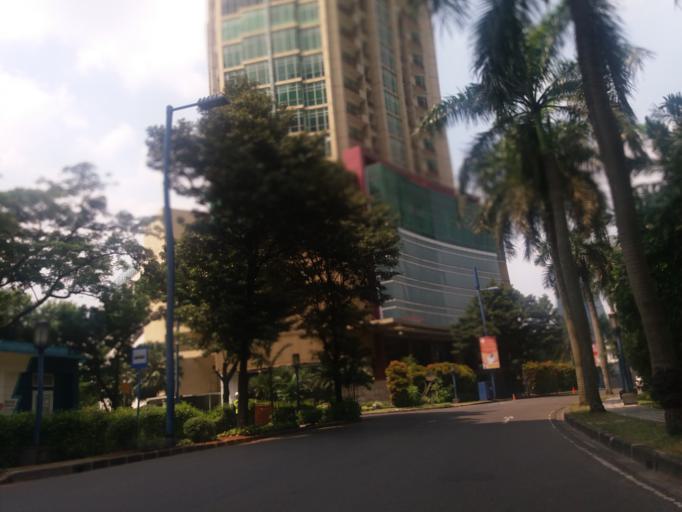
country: ID
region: Jakarta Raya
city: Jakarta
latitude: -6.2279
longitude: 106.8274
